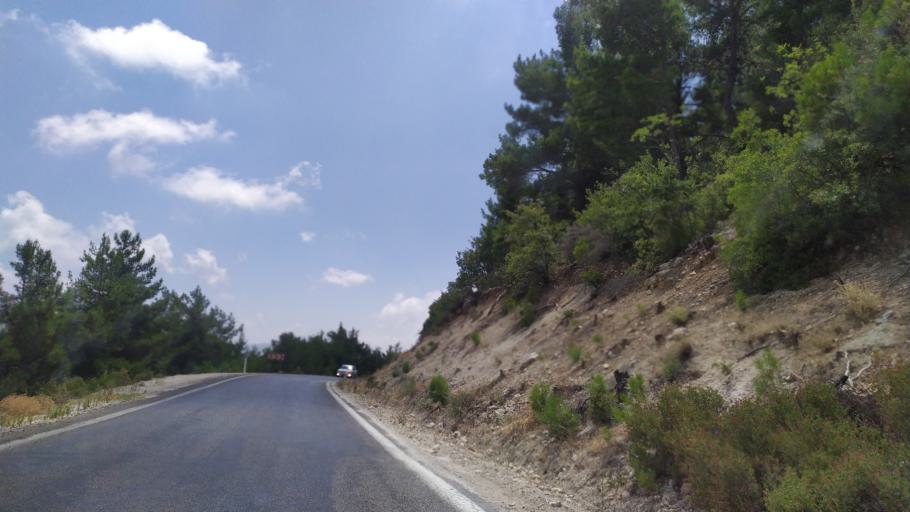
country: TR
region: Mersin
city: Gulnar
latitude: 36.2963
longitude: 33.3798
